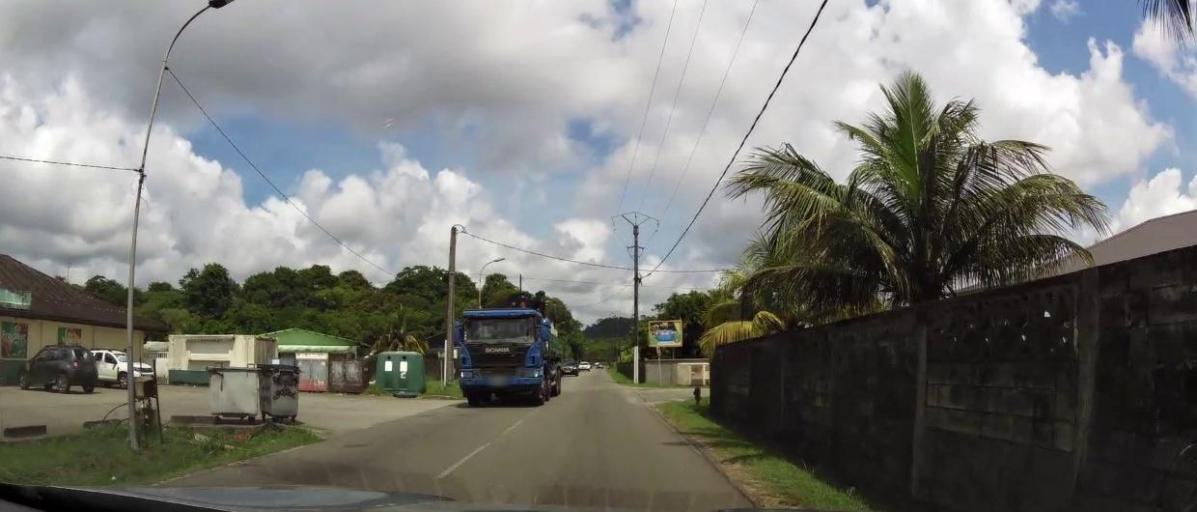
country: GF
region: Guyane
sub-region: Guyane
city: Matoury
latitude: 4.8753
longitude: -52.3342
